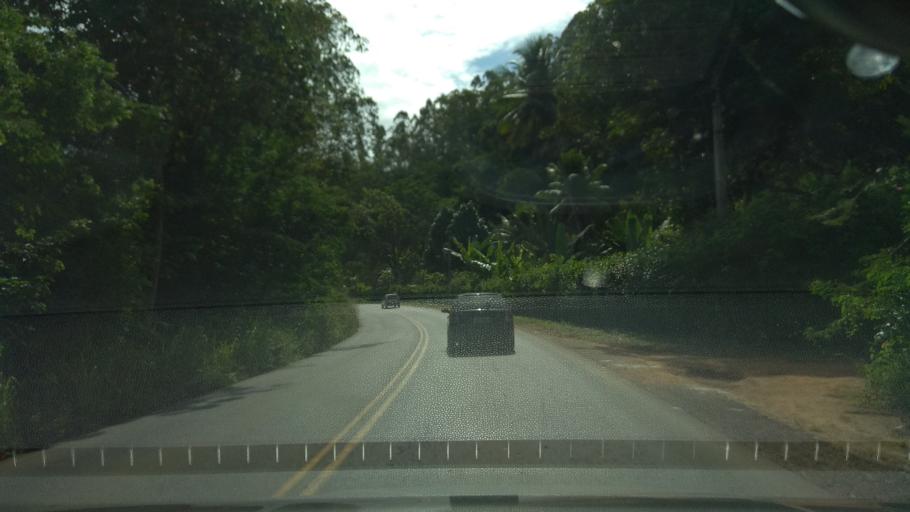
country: BR
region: Bahia
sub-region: Ubaira
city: Ubaira
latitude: -13.2630
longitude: -39.6188
